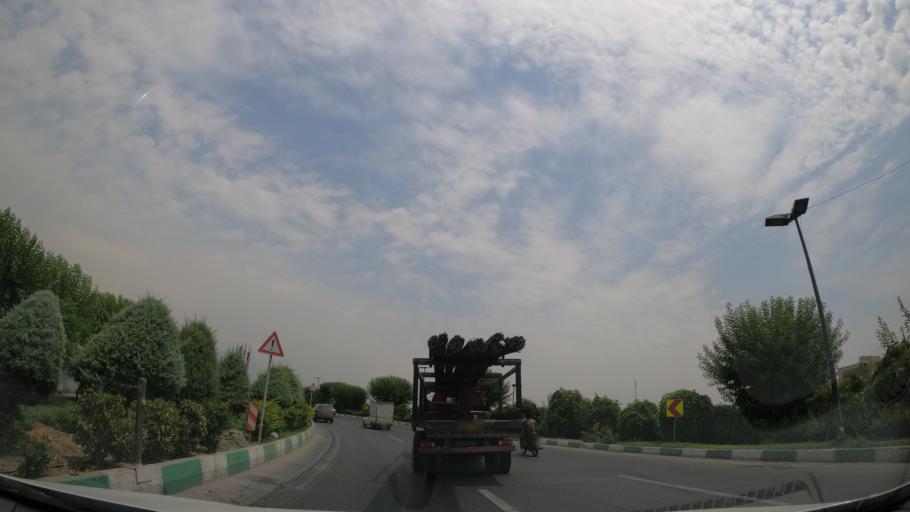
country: IR
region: Tehran
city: Tehran
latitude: 35.6786
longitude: 51.3410
